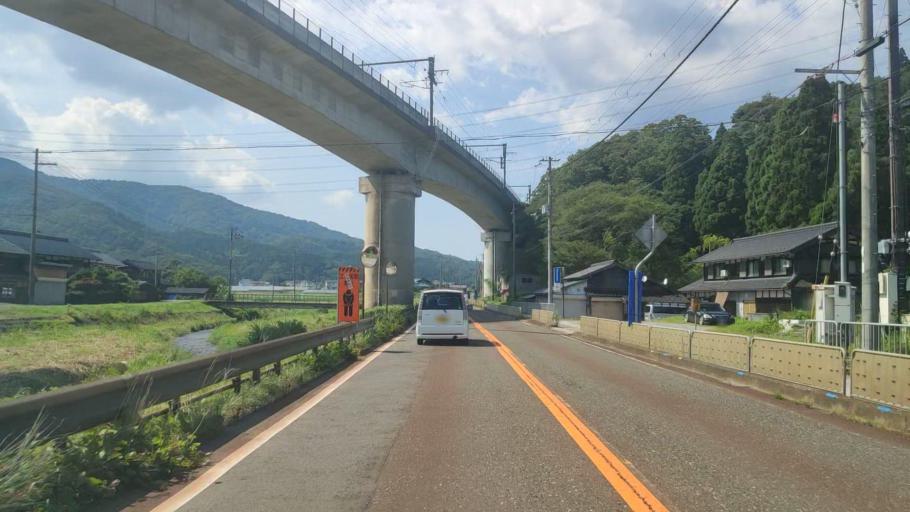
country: JP
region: Fukui
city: Tsuruga
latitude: 35.5312
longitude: 136.1552
